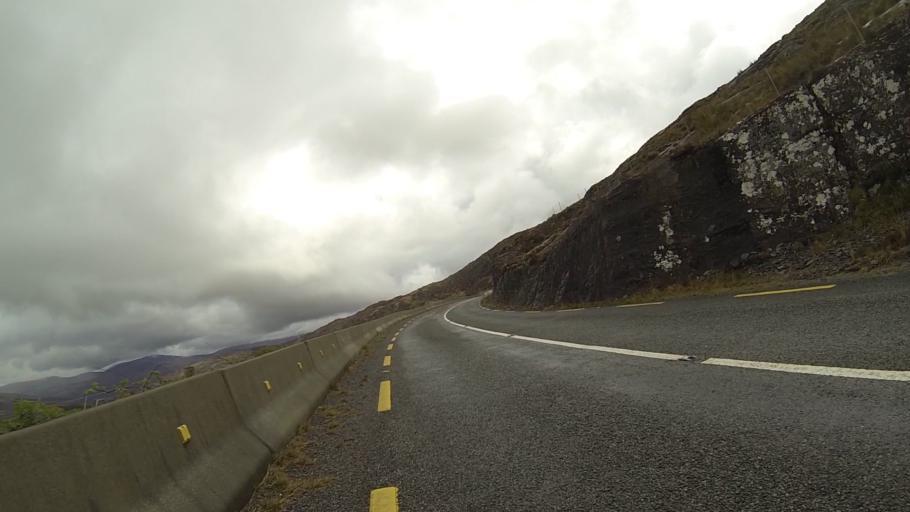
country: IE
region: Munster
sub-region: Ciarrai
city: Kenmare
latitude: 51.7867
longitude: -9.5906
